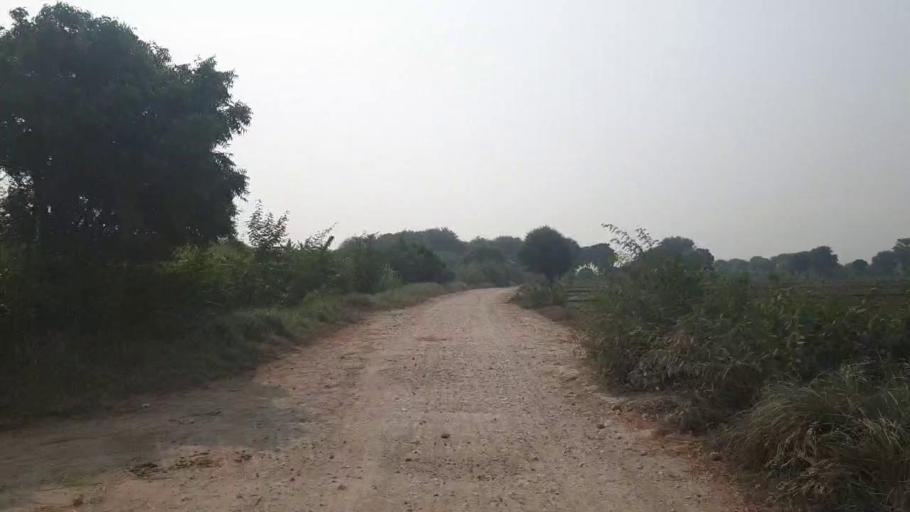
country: PK
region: Sindh
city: Tando Muhammad Khan
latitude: 25.2368
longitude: 68.5704
